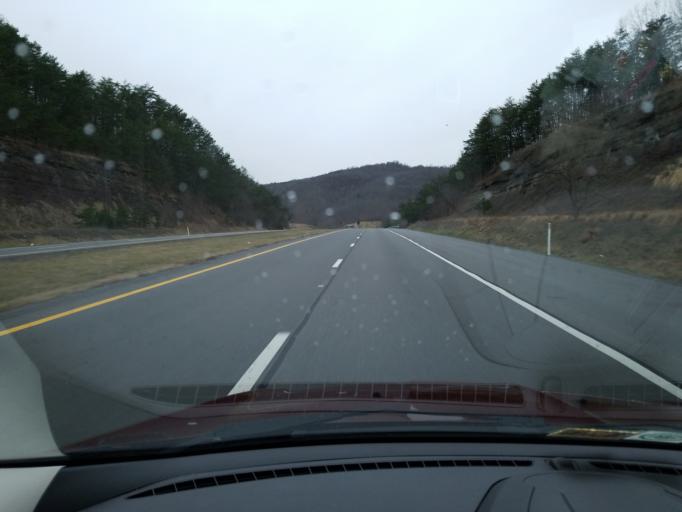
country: US
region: West Virginia
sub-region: Mercer County
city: Athens
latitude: 37.3408
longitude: -80.9765
